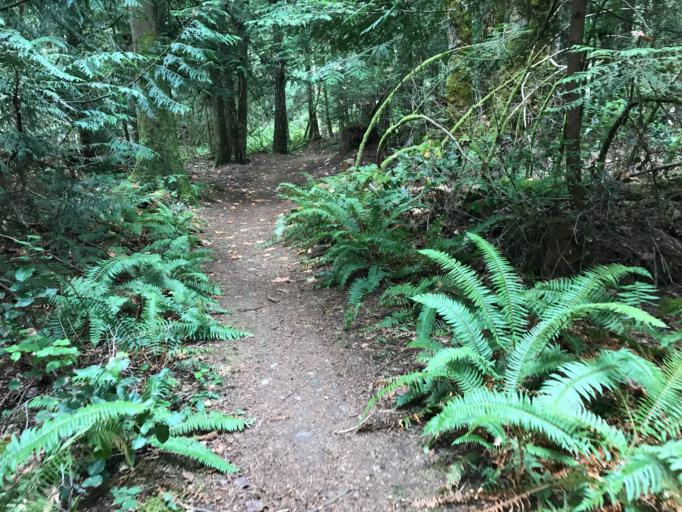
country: CA
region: British Columbia
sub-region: Cowichan Valley Regional District
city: Ladysmith
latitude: 48.9284
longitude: -123.7415
